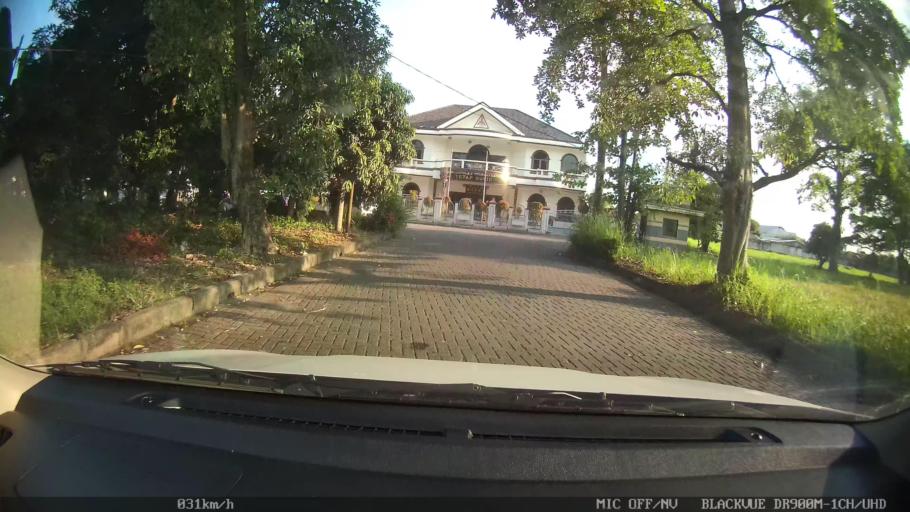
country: ID
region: North Sumatra
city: Medan
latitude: 3.6208
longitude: 98.6535
